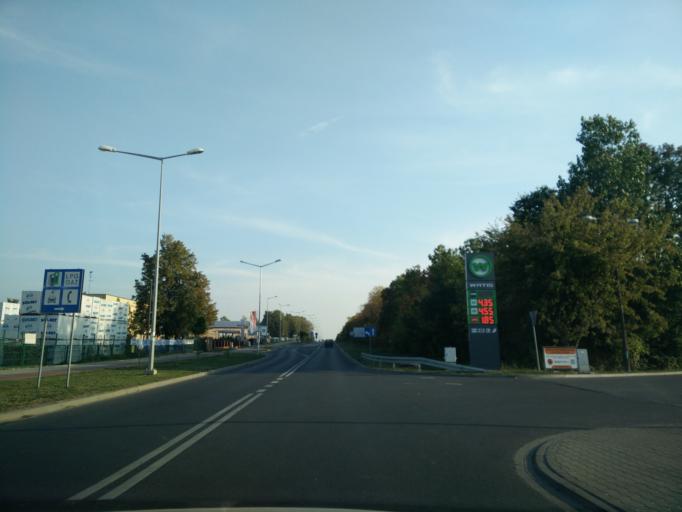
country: PL
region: Greater Poland Voivodeship
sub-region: Powiat sredzki
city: Sroda Wielkopolska
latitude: 52.2204
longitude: 17.2884
